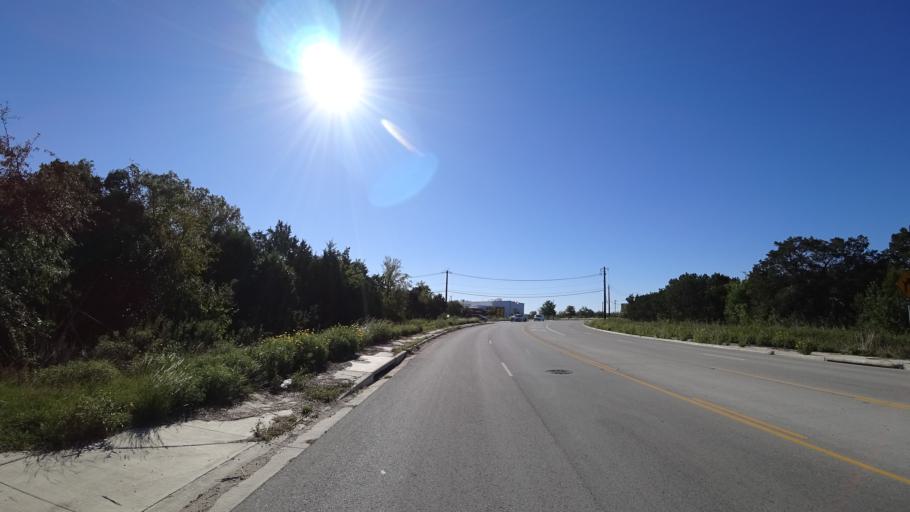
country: US
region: Texas
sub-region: Travis County
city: Austin
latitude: 30.3246
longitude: -97.6589
